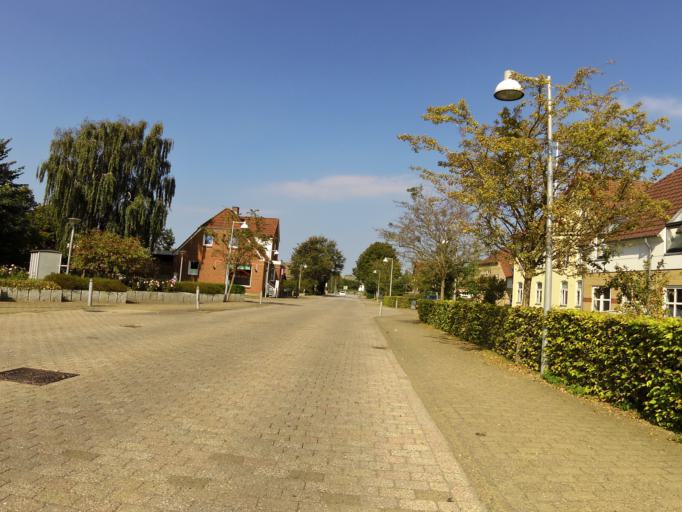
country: DK
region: South Denmark
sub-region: Vejen Kommune
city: Vejen
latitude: 55.4201
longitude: 9.1532
